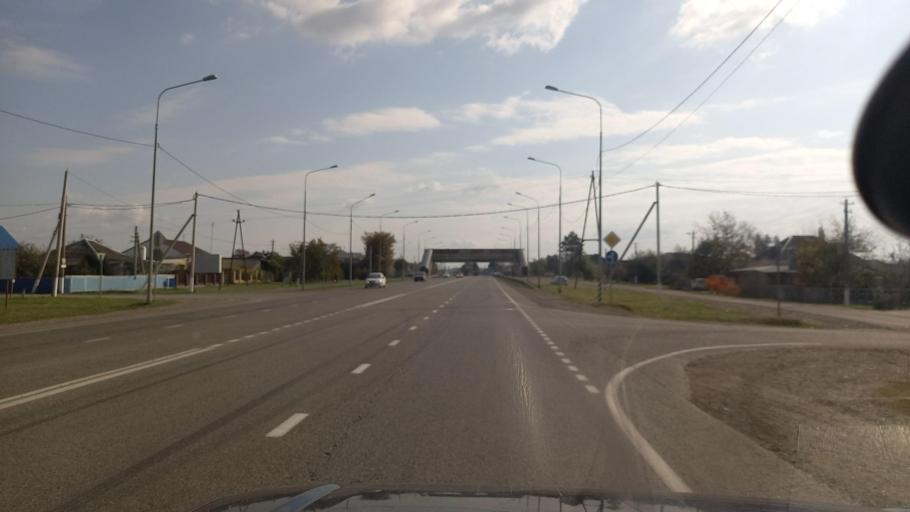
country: RU
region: Krasnodarskiy
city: Novoukrainskiy
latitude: 44.8969
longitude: 38.0479
